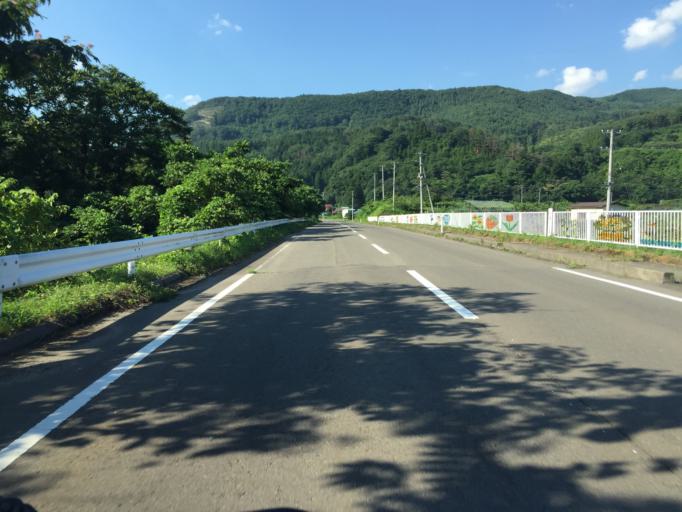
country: JP
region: Fukushima
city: Hobaramachi
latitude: 37.9005
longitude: 140.4312
